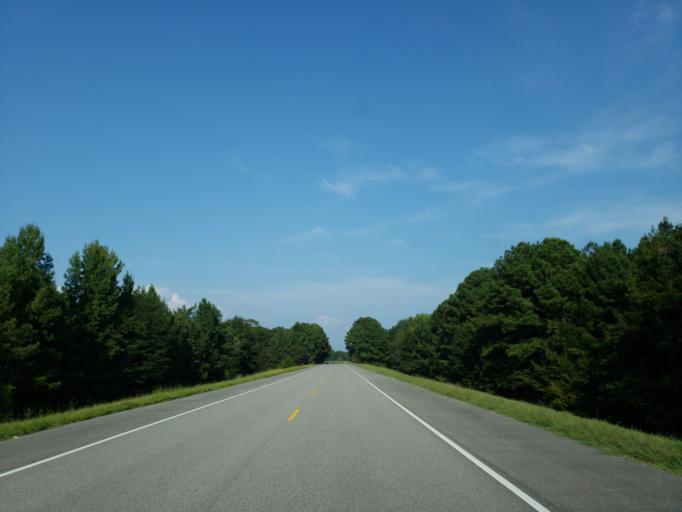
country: US
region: Alabama
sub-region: Sumter County
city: Livingston
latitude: 32.6977
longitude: -88.1047
